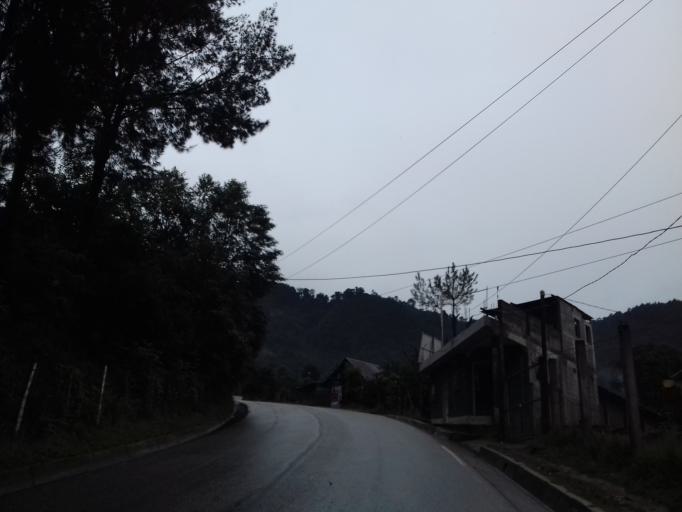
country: GT
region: Quiche
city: Nebaj
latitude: 15.3839
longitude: -91.1115
